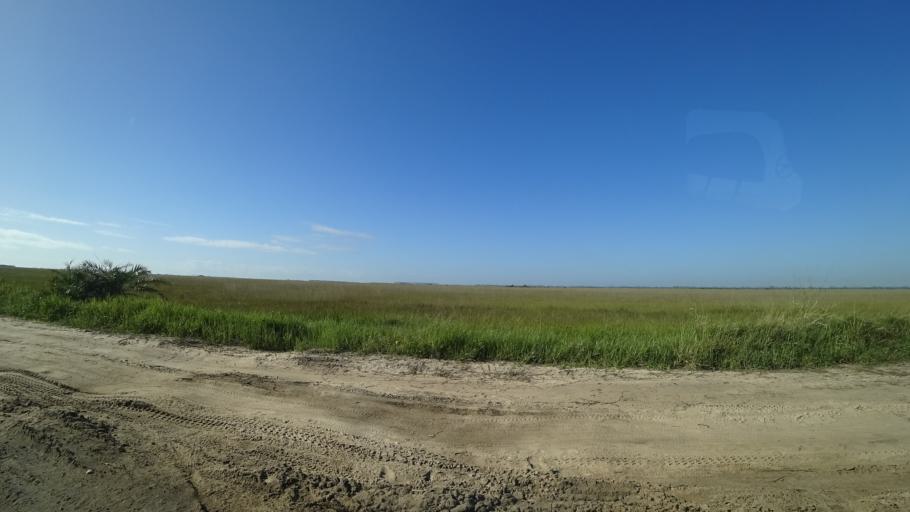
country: MZ
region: Sofala
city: Beira
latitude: -19.7536
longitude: 34.9301
